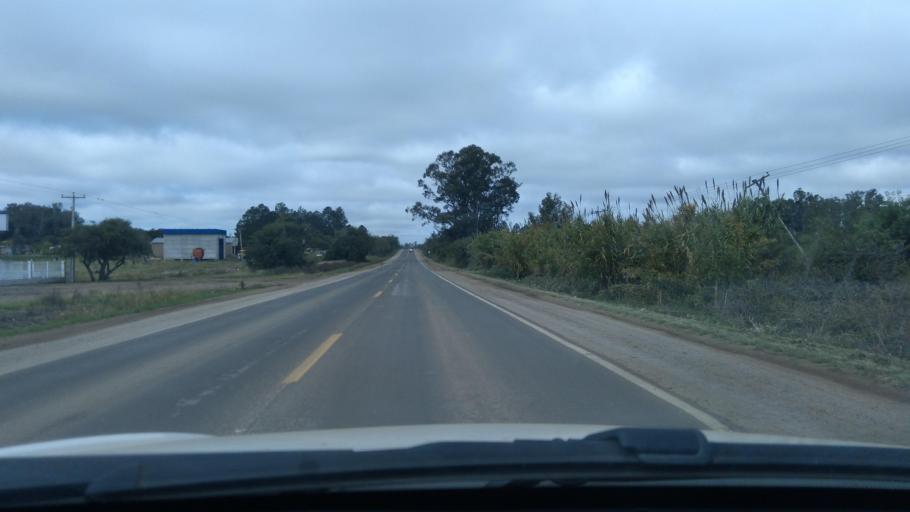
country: BR
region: Rio Grande do Sul
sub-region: Dom Pedrito
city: Dom Pedrito
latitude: -30.9692
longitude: -54.6600
